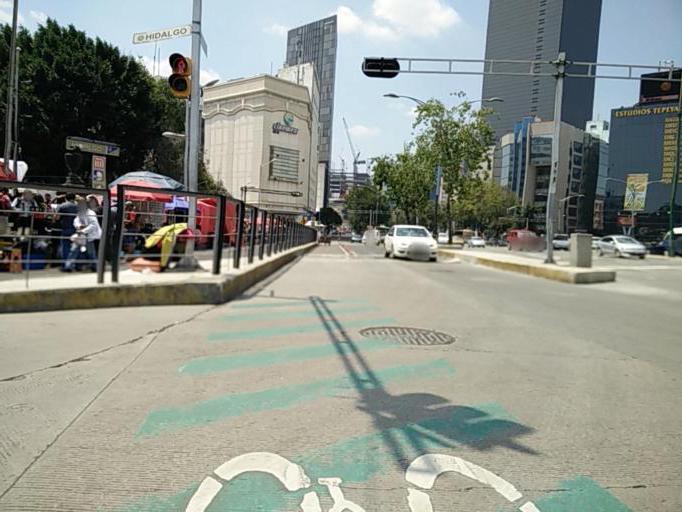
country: MX
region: Mexico City
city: Cuauhtemoc
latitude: 19.4373
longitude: -99.1465
